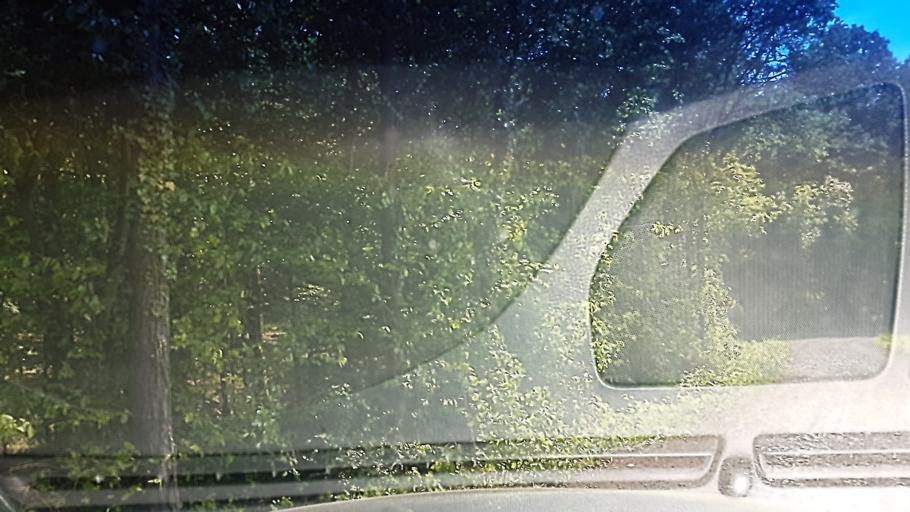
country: DE
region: Bavaria
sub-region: Upper Franconia
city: Buttenheim
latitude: 49.8270
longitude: 11.0598
